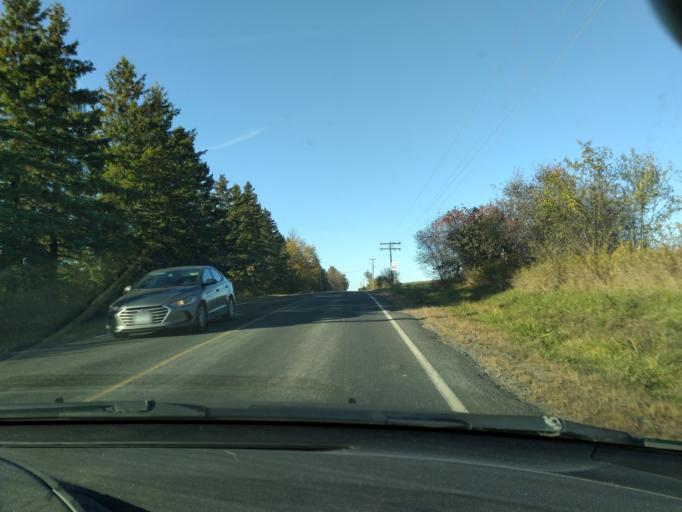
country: CA
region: Ontario
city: Bradford West Gwillimbury
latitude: 43.9280
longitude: -79.7099
